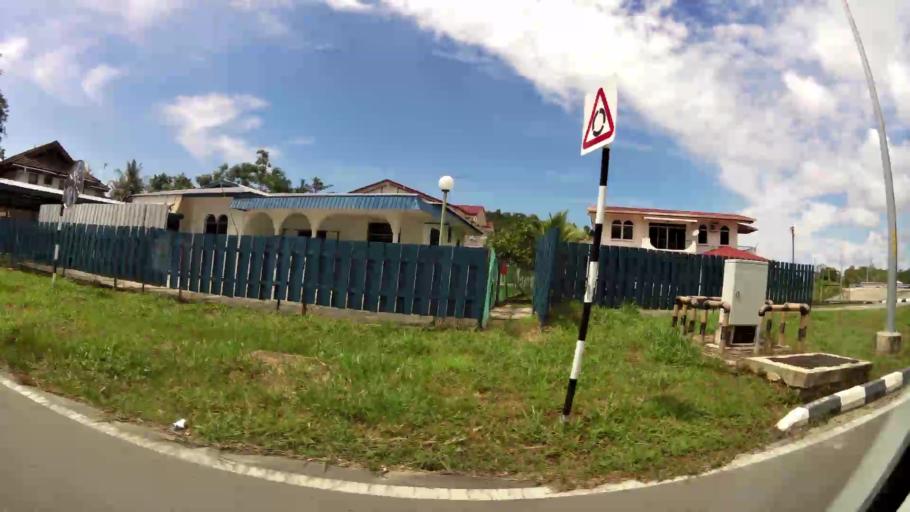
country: BN
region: Brunei and Muara
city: Bandar Seri Begawan
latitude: 4.9902
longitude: 114.9514
